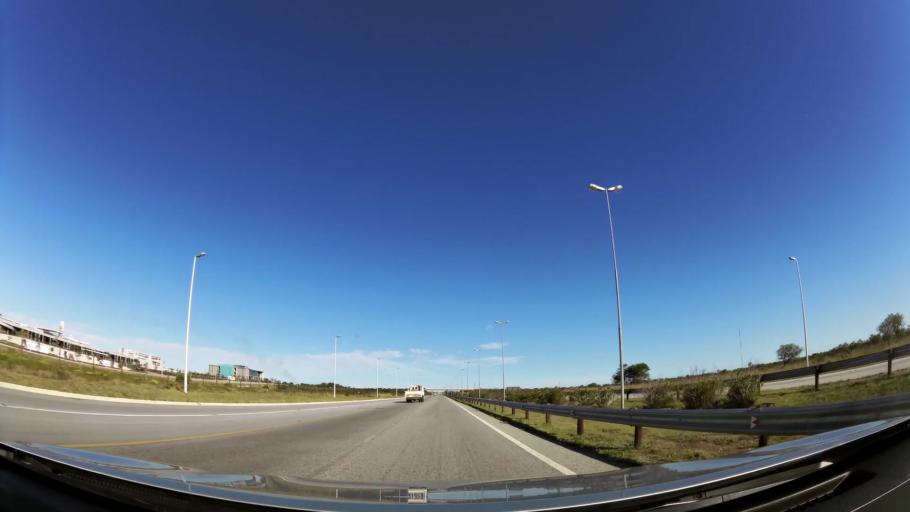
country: ZA
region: Eastern Cape
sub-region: Nelson Mandela Bay Metropolitan Municipality
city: Port Elizabeth
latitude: -33.9474
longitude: 25.4621
